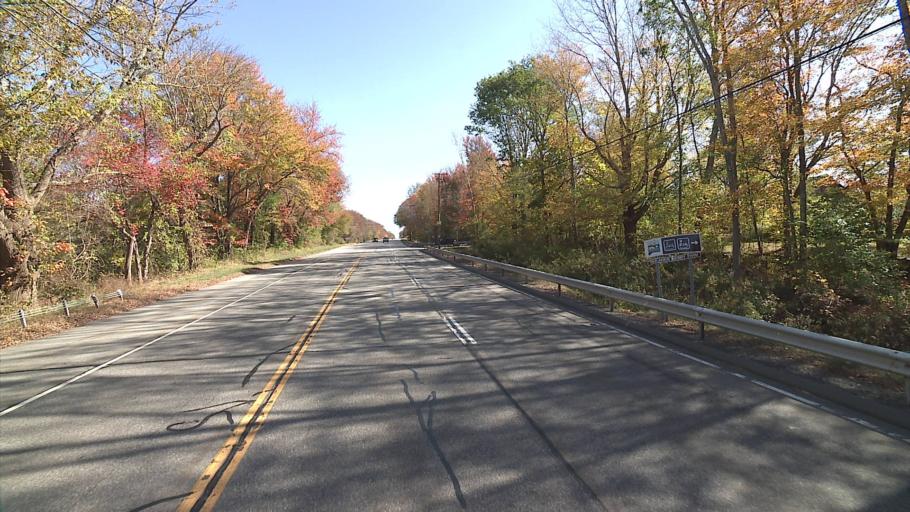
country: US
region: Connecticut
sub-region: Windham County
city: Danielson
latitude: 41.7909
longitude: -71.8269
